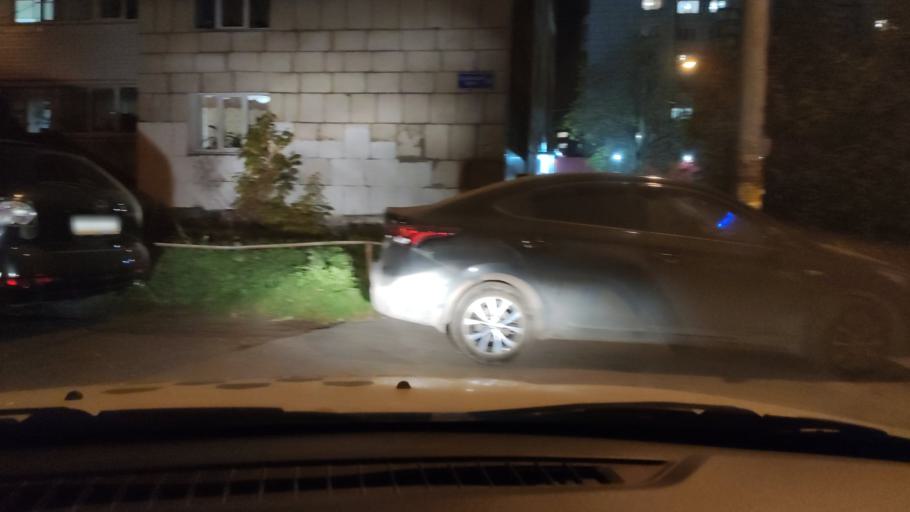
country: RU
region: Perm
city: Perm
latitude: 57.9786
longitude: 56.2335
